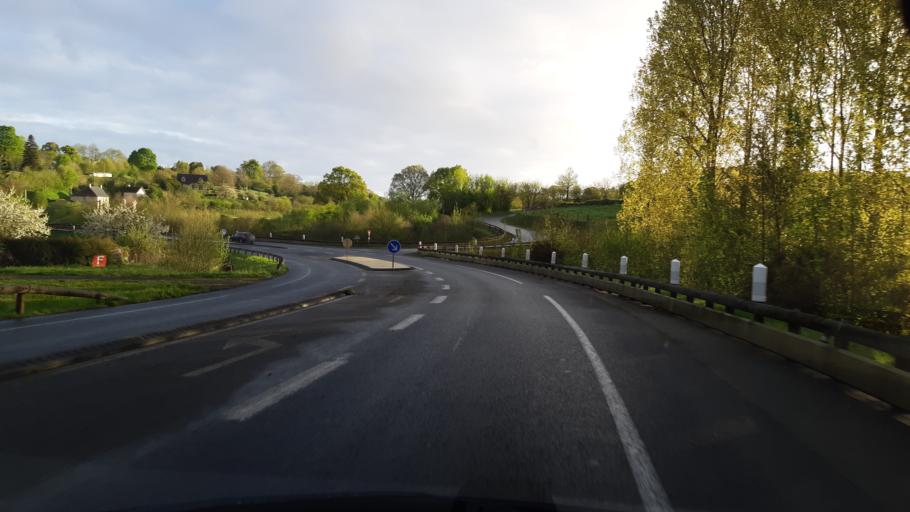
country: FR
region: Lower Normandy
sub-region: Departement de la Manche
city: Agneaux
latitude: 49.0688
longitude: -1.1300
